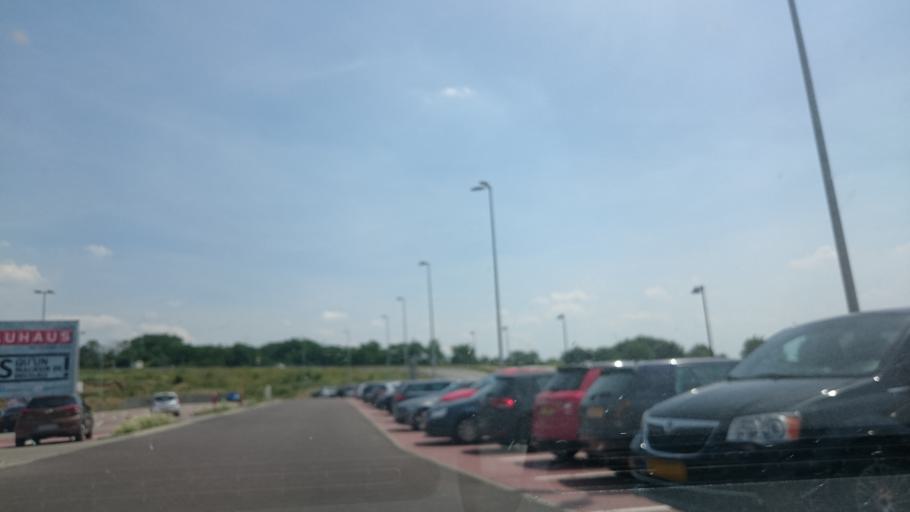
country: LU
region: Luxembourg
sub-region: Canton de Capellen
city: Mamer
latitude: 49.6401
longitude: 6.0150
